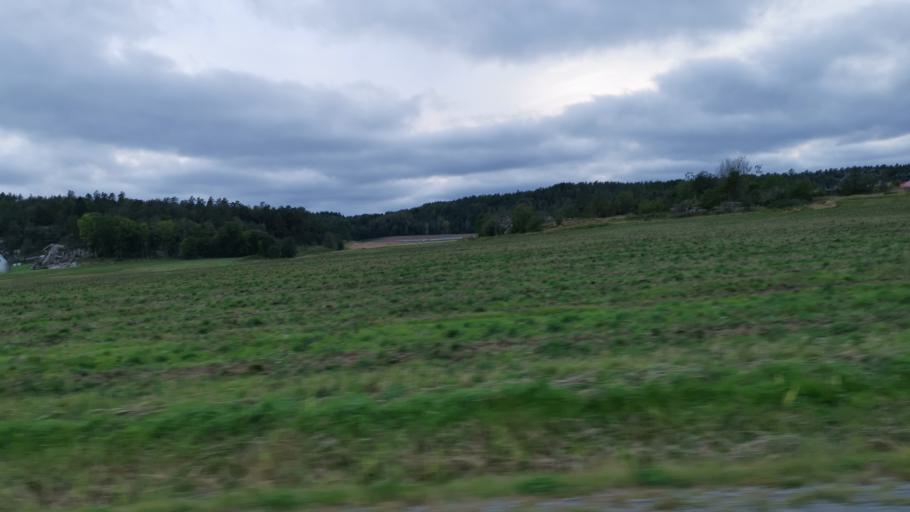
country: SE
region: Vaestra Goetaland
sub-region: Tanums Kommun
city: Tanumshede
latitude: 58.6662
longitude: 11.3442
